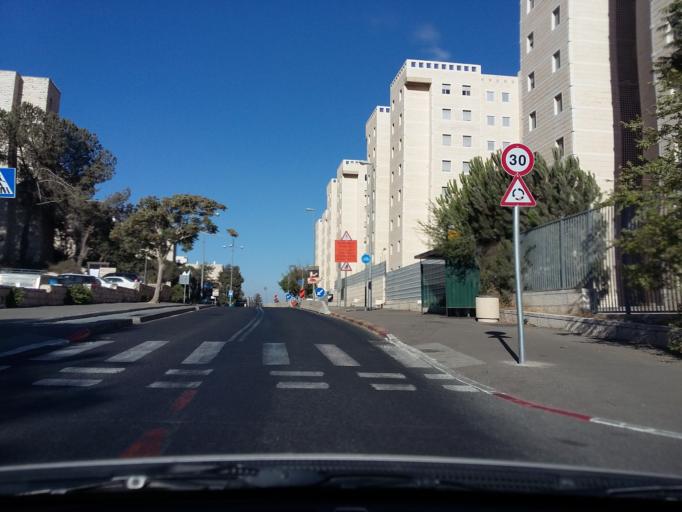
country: PS
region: West Bank
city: East Jerusalem
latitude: 31.8008
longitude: 35.2374
